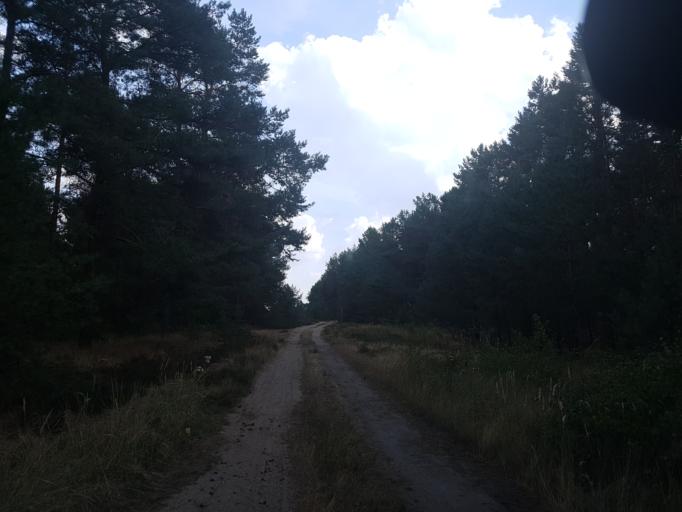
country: DE
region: Brandenburg
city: Treuenbrietzen
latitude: 52.0561
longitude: 12.8373
